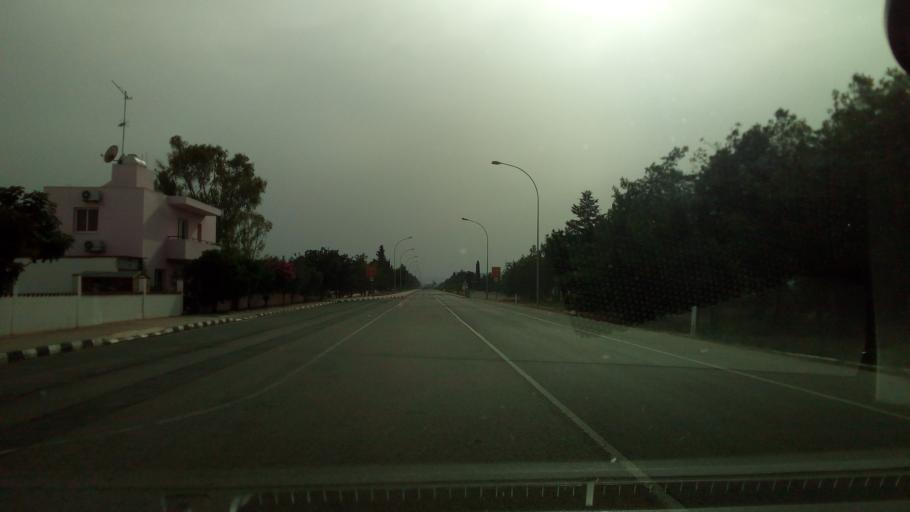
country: CY
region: Larnaka
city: Pyla
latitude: 34.9826
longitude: 33.6955
